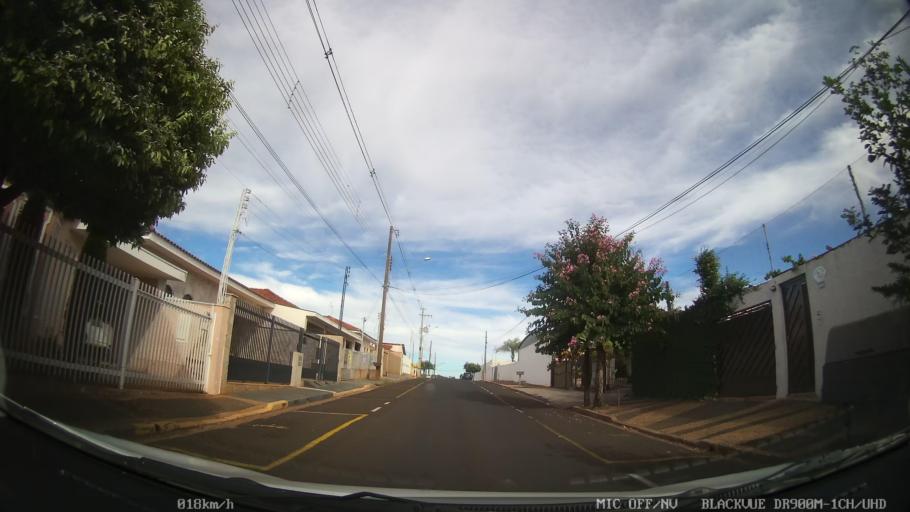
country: BR
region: Sao Paulo
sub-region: Catanduva
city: Catanduva
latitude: -21.1472
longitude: -48.9838
